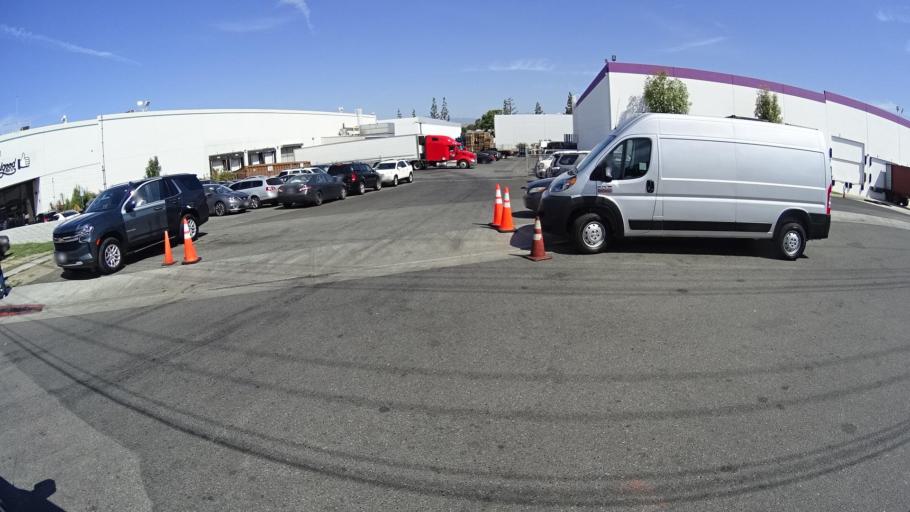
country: US
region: California
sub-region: Los Angeles County
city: South San Jose Hills
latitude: 33.9977
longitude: -117.8903
